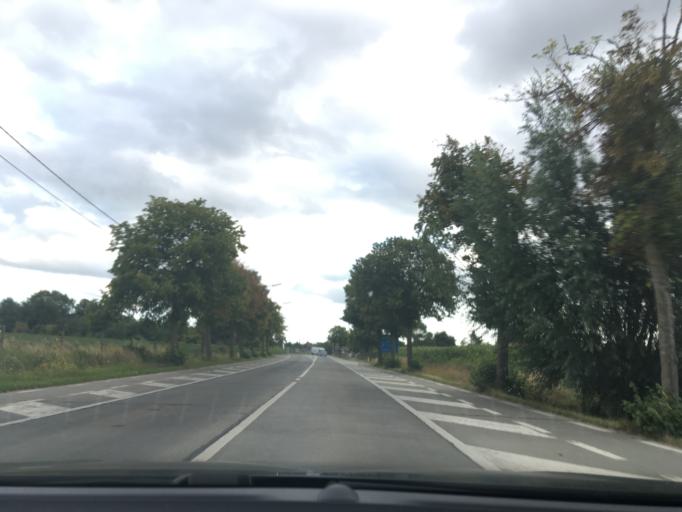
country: BE
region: Flanders
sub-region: Provincie West-Vlaanderen
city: Zonnebeke
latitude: 50.9015
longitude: 2.9407
